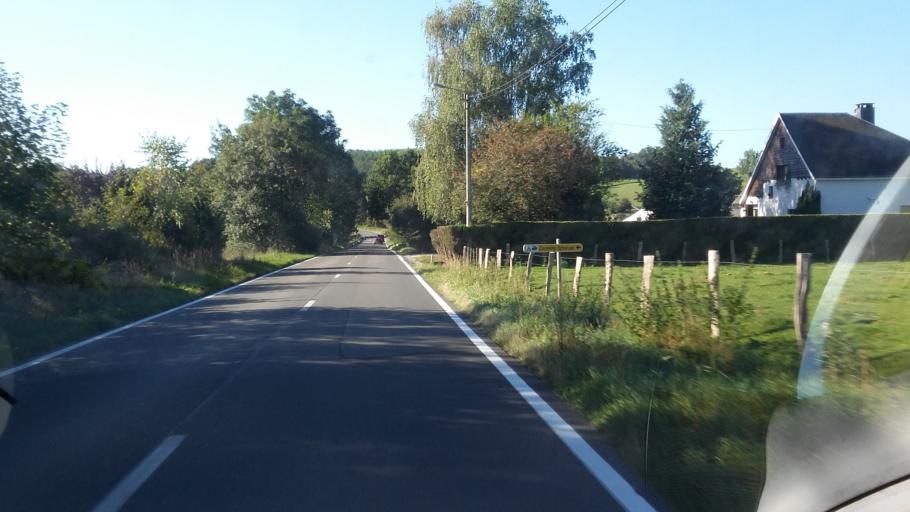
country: BE
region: Wallonia
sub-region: Province du Luxembourg
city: Neufchateau
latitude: 49.8340
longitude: 5.4158
